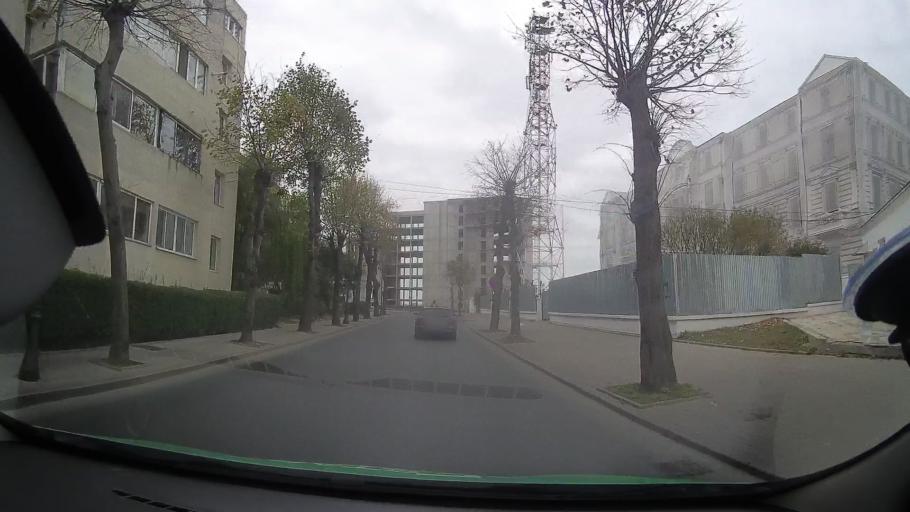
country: RO
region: Constanta
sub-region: Municipiul Constanta
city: Constanta
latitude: 44.1721
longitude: 28.6644
